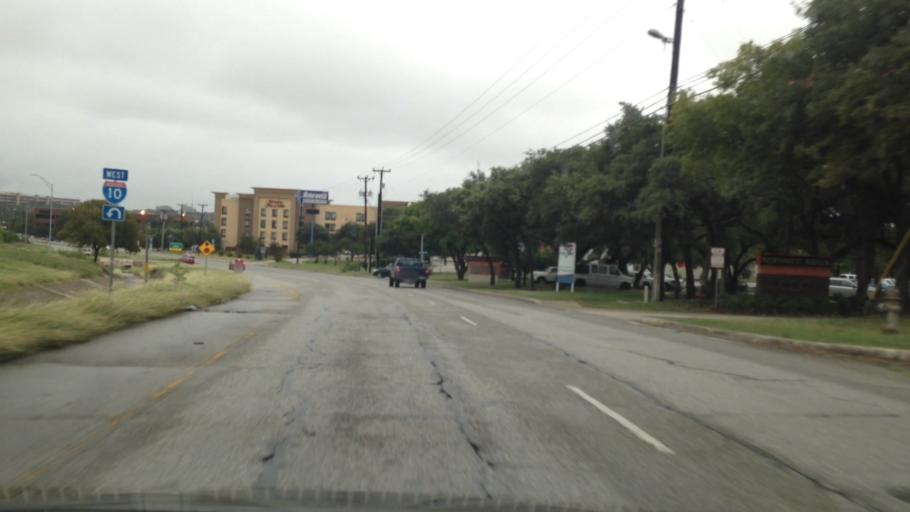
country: US
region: Texas
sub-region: Bexar County
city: Shavano Park
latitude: 29.5502
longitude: -98.5864
